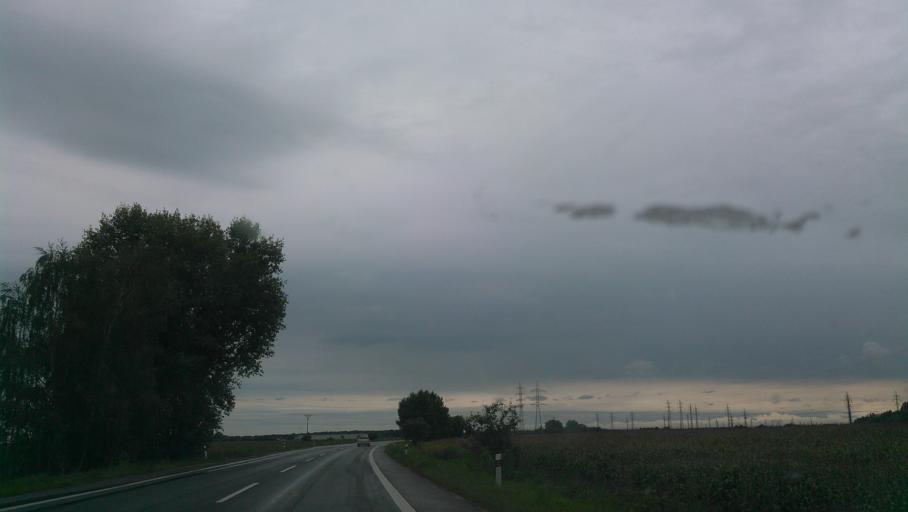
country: SK
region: Trnavsky
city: Dunajska Streda
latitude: 47.9784
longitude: 17.5960
